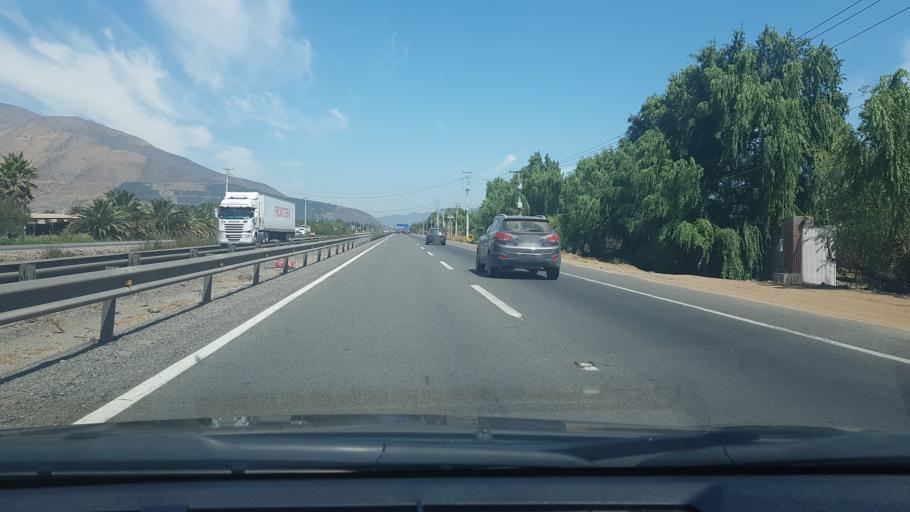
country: CL
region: Valparaiso
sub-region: Provincia de San Felipe
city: Llaillay
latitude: -32.8475
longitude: -70.9655
